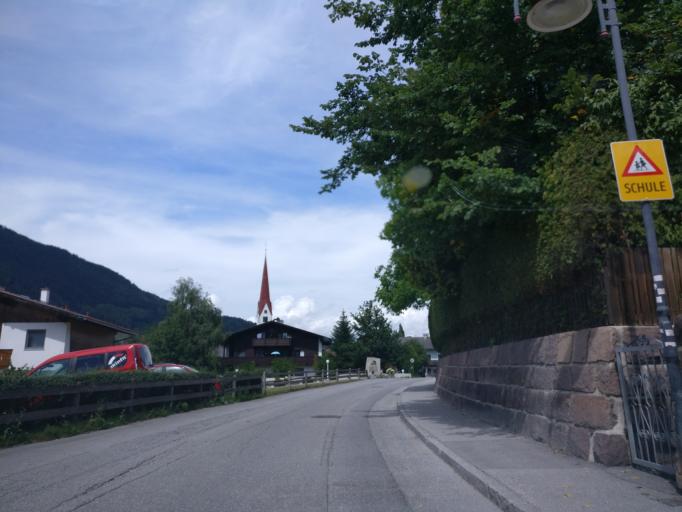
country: AT
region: Tyrol
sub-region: Politischer Bezirk Innsbruck Land
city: Mieders
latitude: 47.1669
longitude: 11.3793
